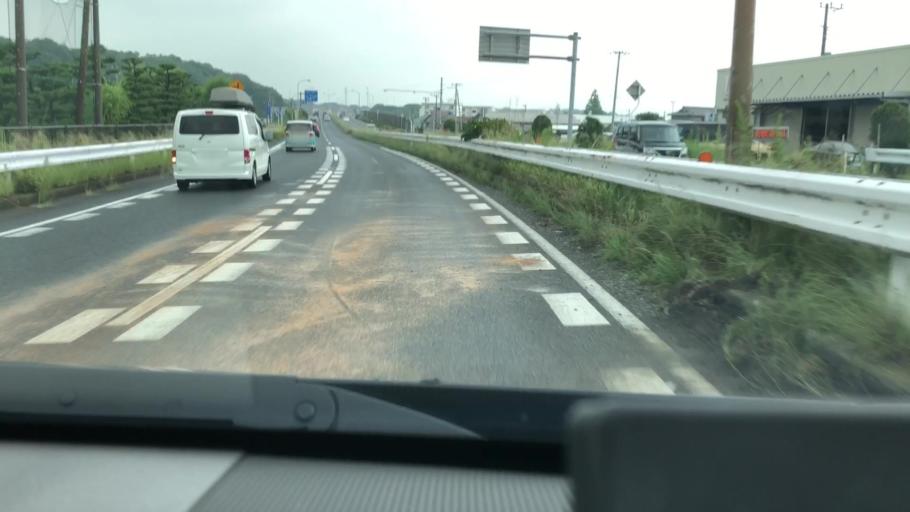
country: JP
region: Chiba
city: Kisarazu
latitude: 35.4418
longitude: 139.9717
